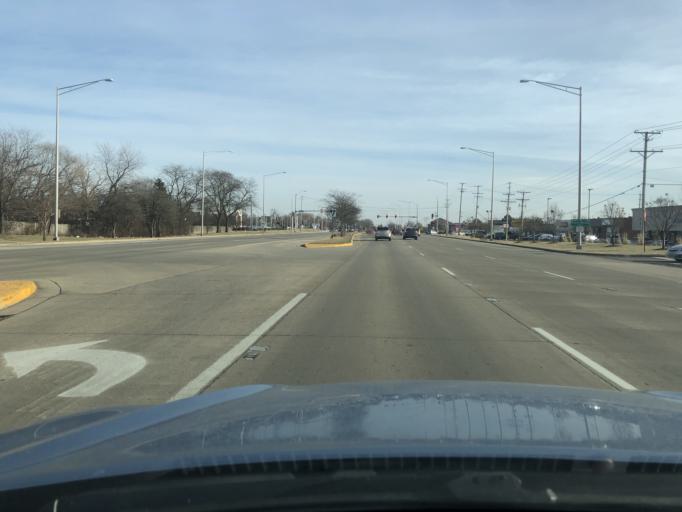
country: US
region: Illinois
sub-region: Cook County
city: Hoffman Estates
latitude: 42.0502
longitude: -88.1018
